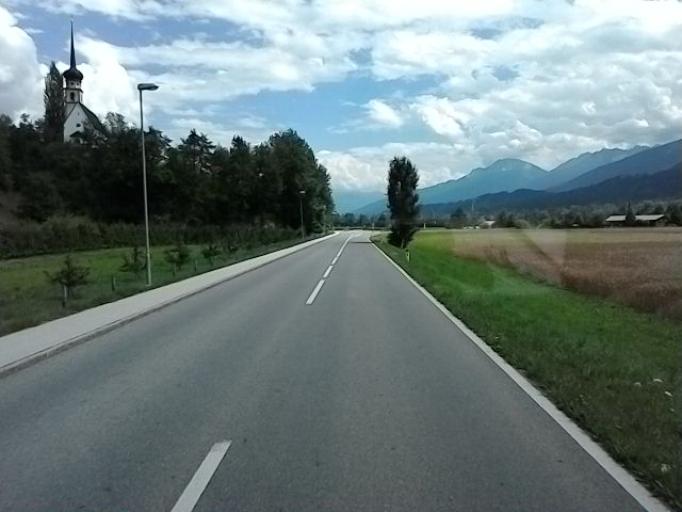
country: AT
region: Tyrol
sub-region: Politischer Bezirk Innsbruck Land
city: Hatting
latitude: 47.2896
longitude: 11.1669
